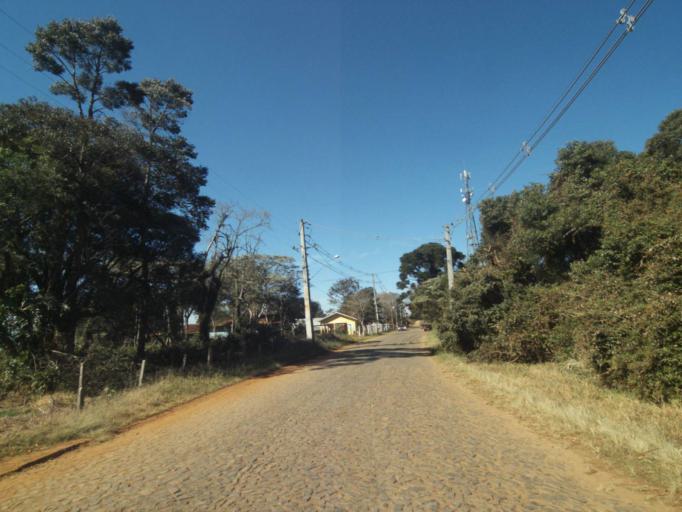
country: BR
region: Parana
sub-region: Reserva
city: Reserva
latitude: -24.6212
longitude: -50.6374
